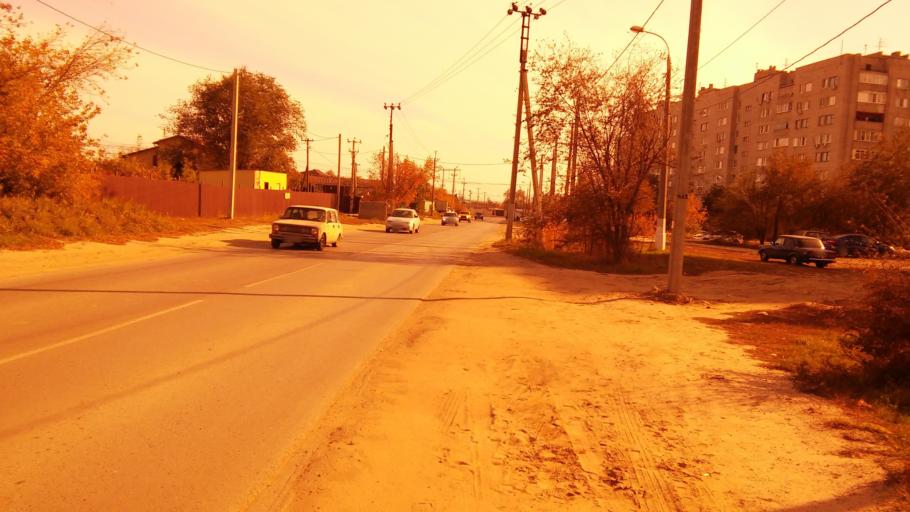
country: RU
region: Volgograd
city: Vodstroy
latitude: 48.8431
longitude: 44.6433
